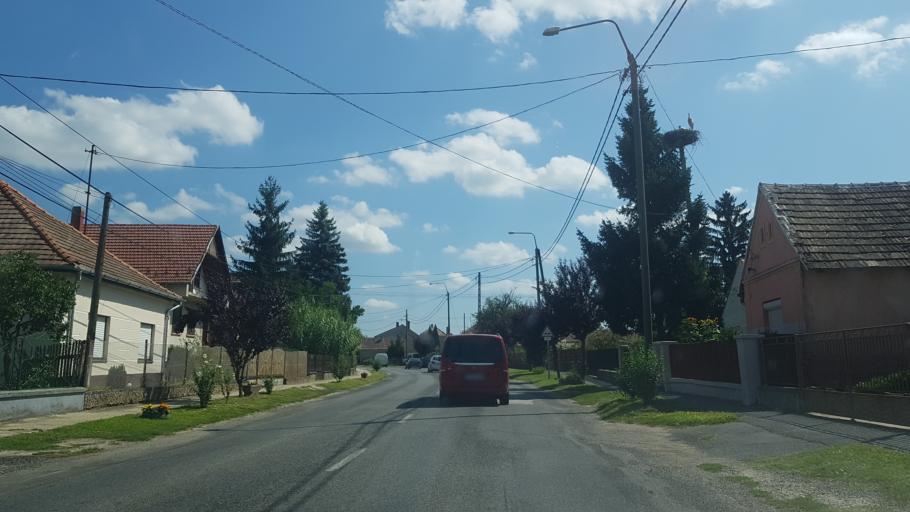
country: HU
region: Somogy
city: Marcali
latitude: 46.5231
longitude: 17.4188
